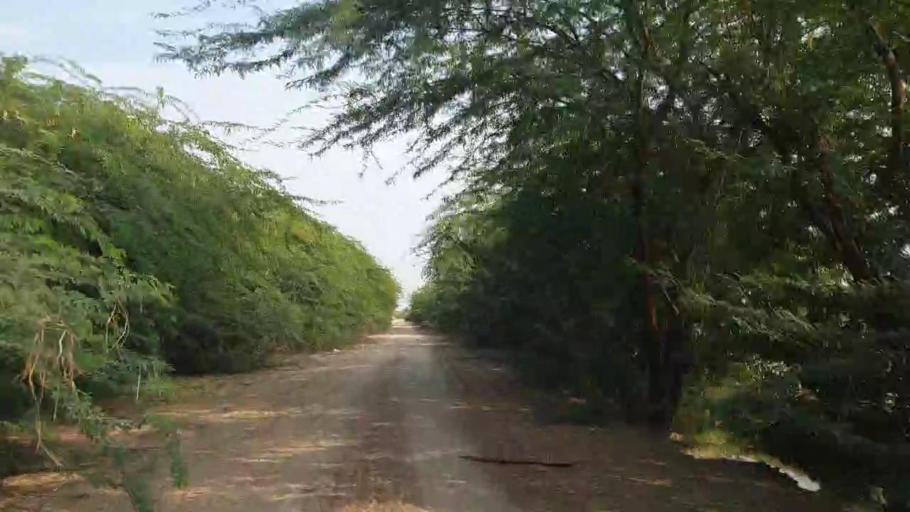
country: PK
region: Sindh
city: Kadhan
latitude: 24.4596
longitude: 68.7953
